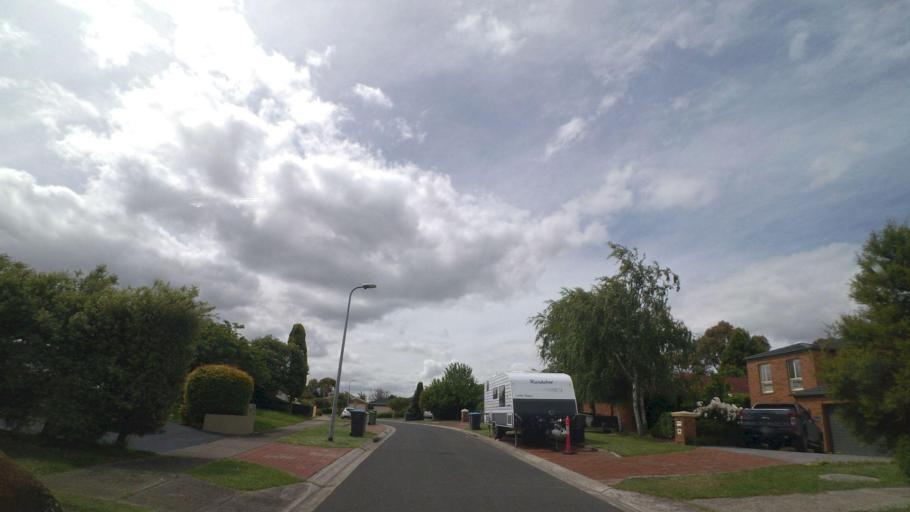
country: AU
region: Victoria
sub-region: Knox
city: Knoxfield
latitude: -37.8891
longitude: 145.2391
